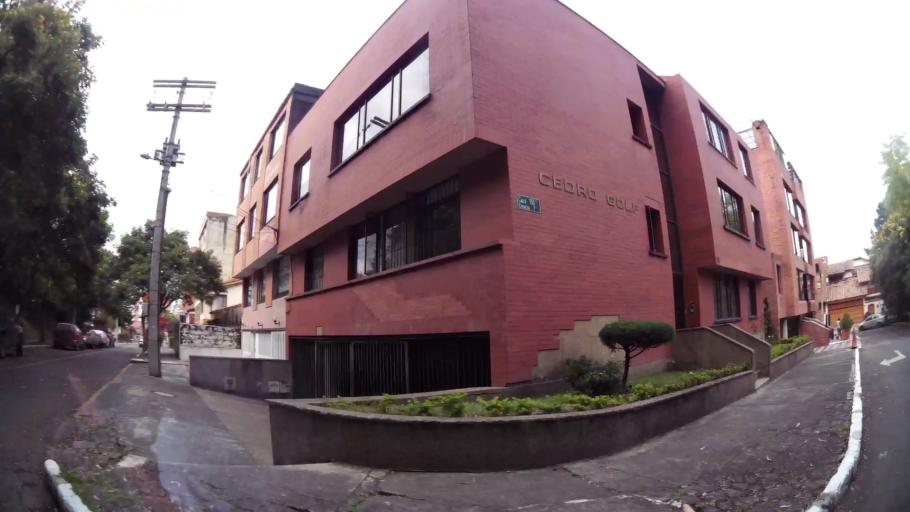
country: CO
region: Bogota D.C.
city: Barrio San Luis
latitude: 4.7266
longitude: -74.0289
